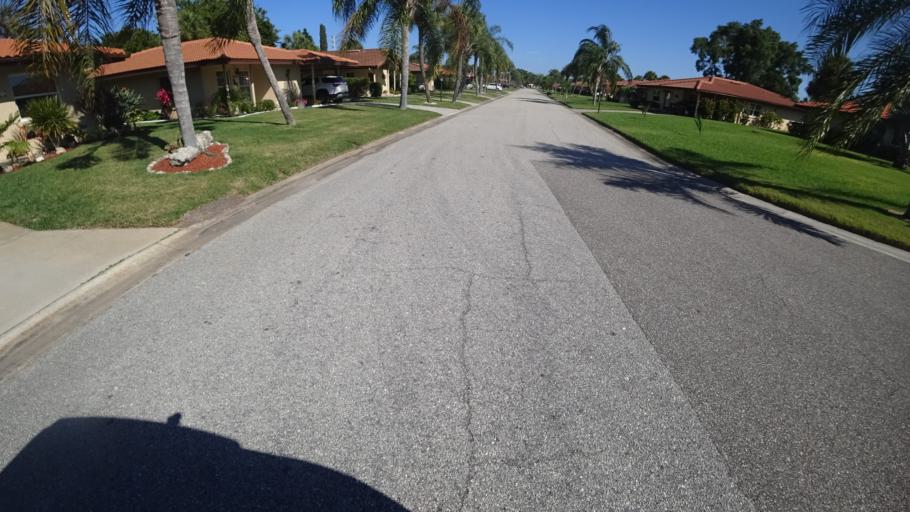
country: US
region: Florida
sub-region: Manatee County
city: Bayshore Gardens
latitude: 27.4263
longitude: -82.5954
